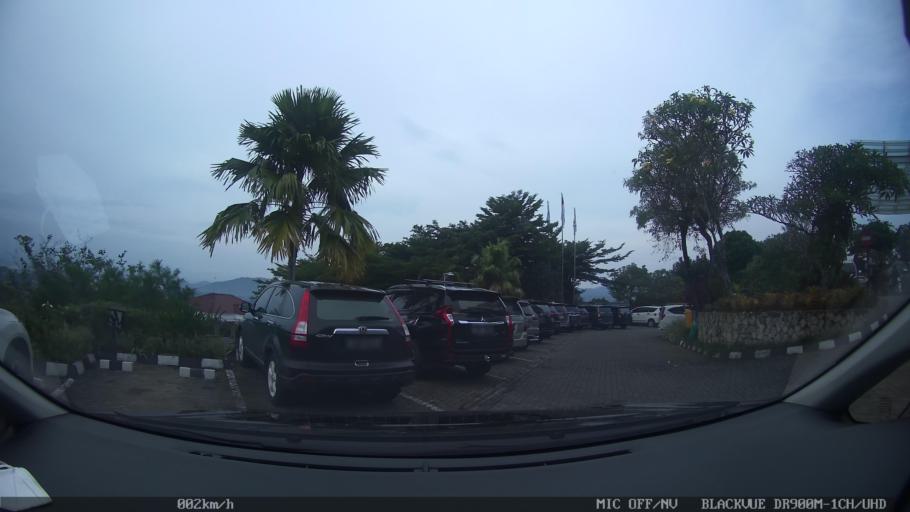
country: ID
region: Lampung
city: Bandarlampung
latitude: -5.4266
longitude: 105.2510
